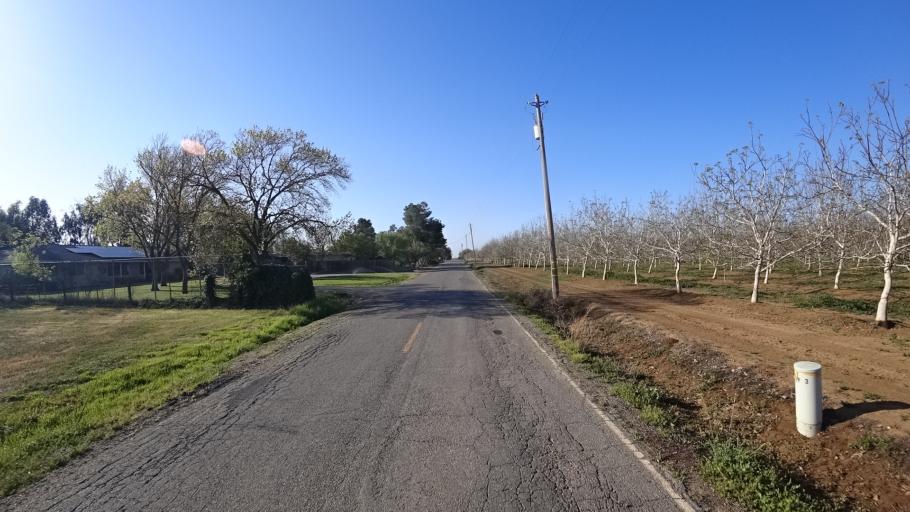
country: US
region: California
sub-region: Glenn County
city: Willows
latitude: 39.5137
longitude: -122.2299
